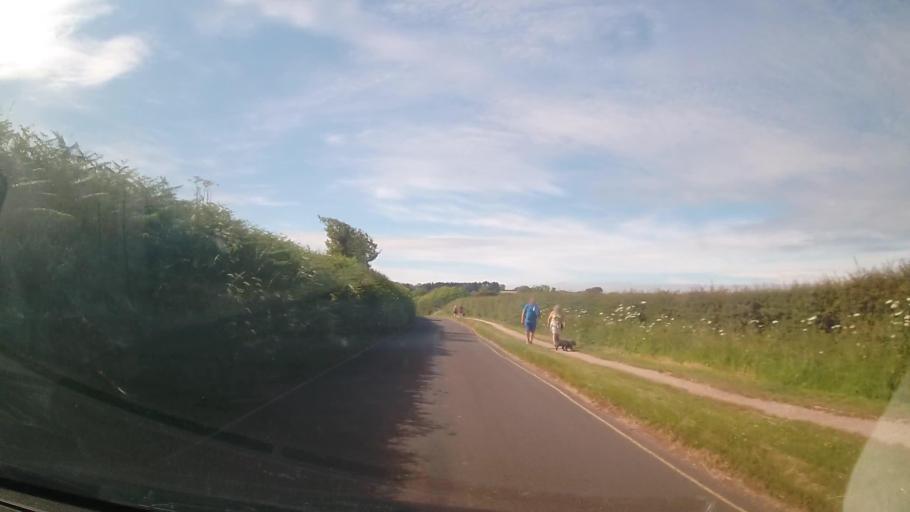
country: GB
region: England
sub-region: Devon
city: Dartmouth
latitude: 50.2893
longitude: -3.6500
